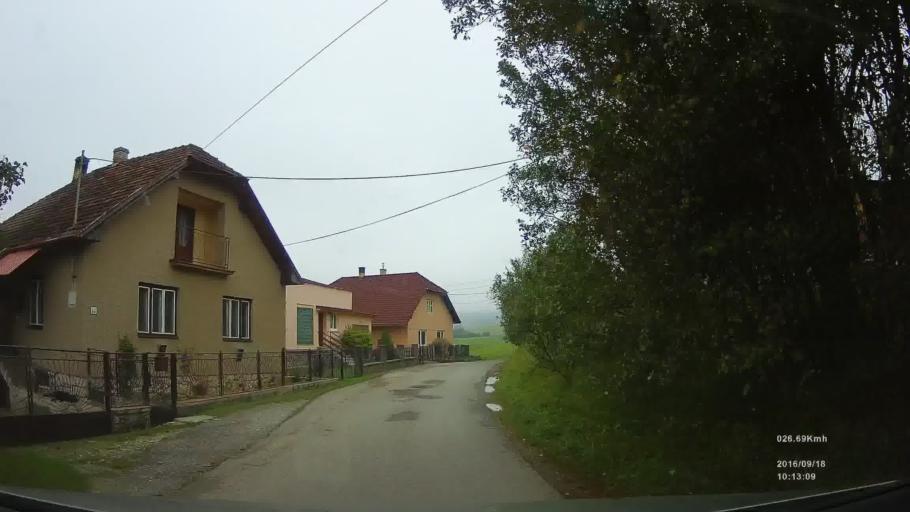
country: SK
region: Kosicky
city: Spisska Nova Ves
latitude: 48.9352
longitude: 20.6329
